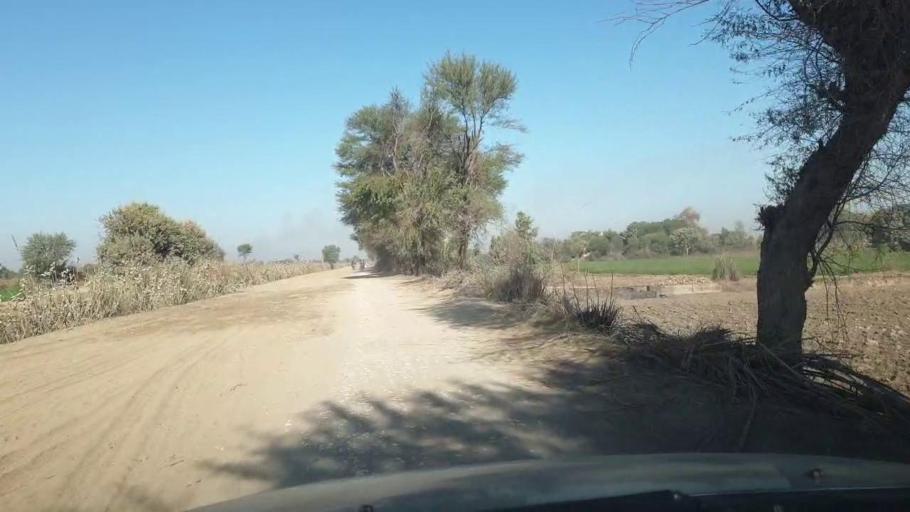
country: PK
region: Sindh
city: Ghotki
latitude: 28.0760
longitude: 69.3469
